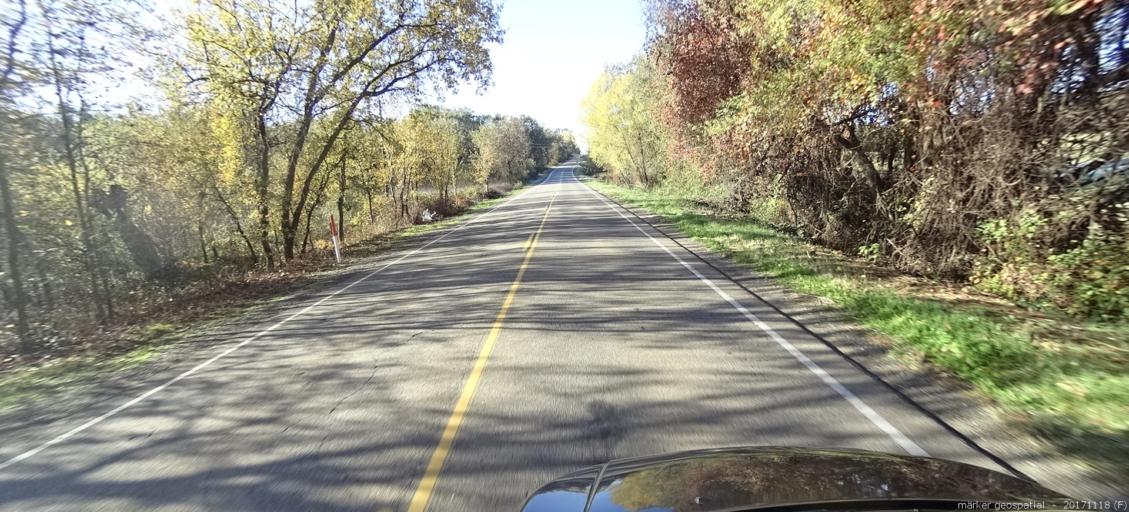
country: US
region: California
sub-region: Shasta County
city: Anderson
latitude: 40.4421
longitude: -122.2646
